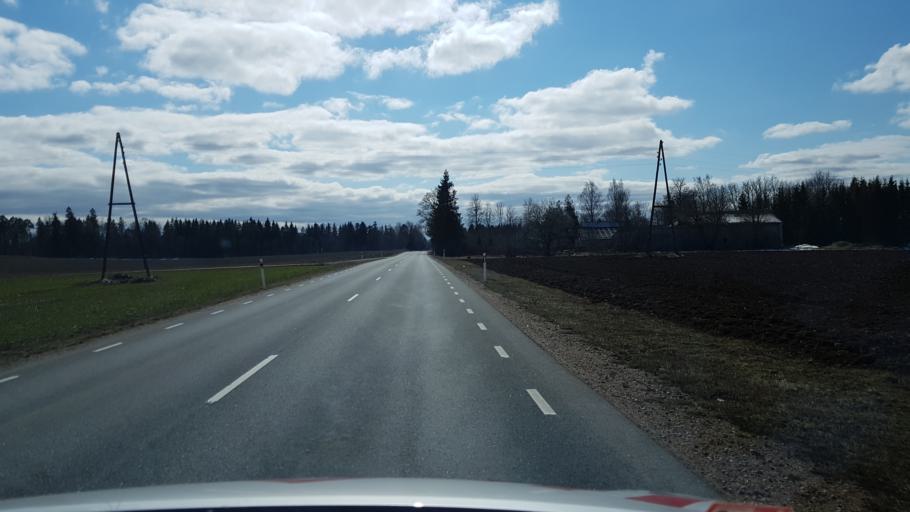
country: EE
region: Laeaene-Virumaa
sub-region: Tapa vald
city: Tapa
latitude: 59.3650
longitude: 26.0010
